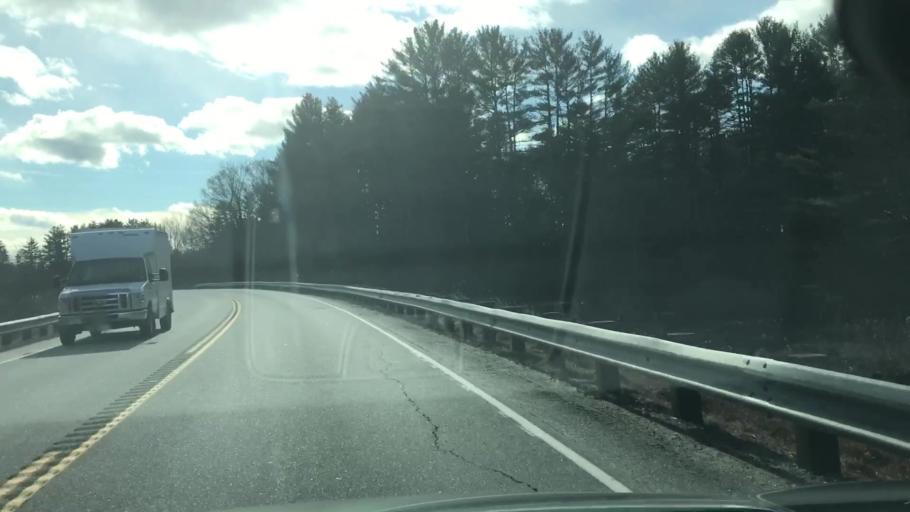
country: US
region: New Hampshire
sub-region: Merrimack County
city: Chichester
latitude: 43.2529
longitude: -71.3740
